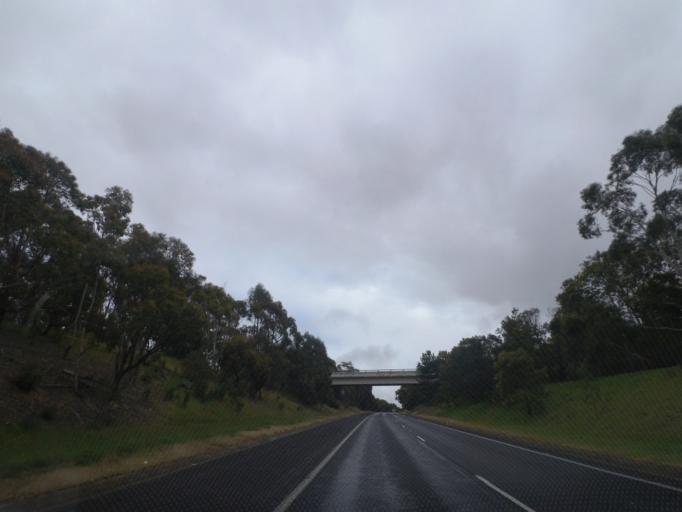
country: AU
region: Victoria
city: Black Hill
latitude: -37.5389
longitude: 143.8814
